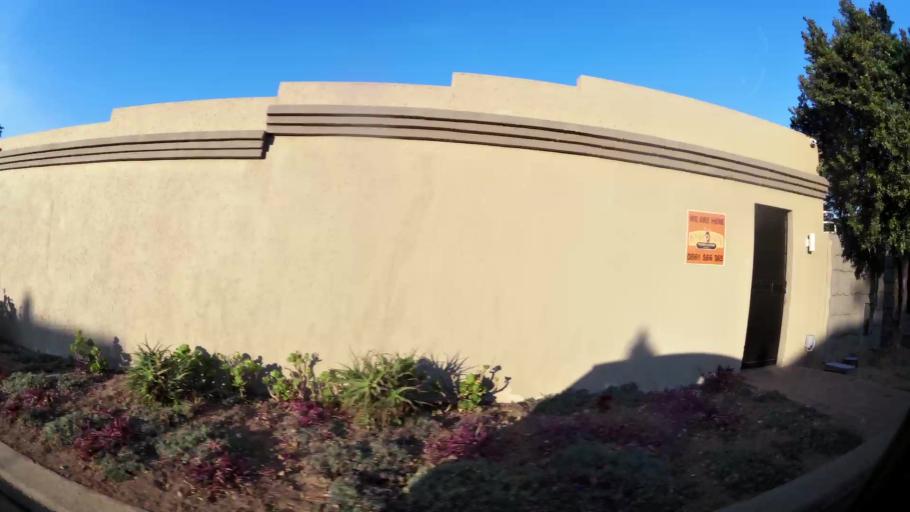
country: ZA
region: Gauteng
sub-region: City of Johannesburg Metropolitan Municipality
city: Diepsloot
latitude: -26.0387
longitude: 27.9769
